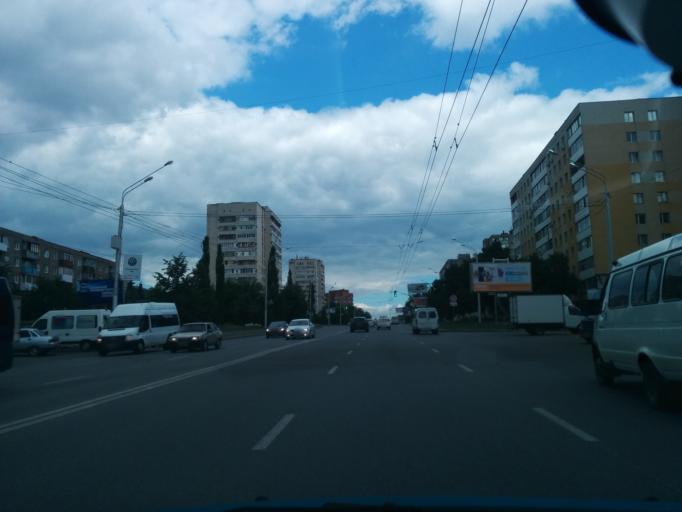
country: RU
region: Bashkortostan
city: Ufa
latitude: 54.7279
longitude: 55.9772
